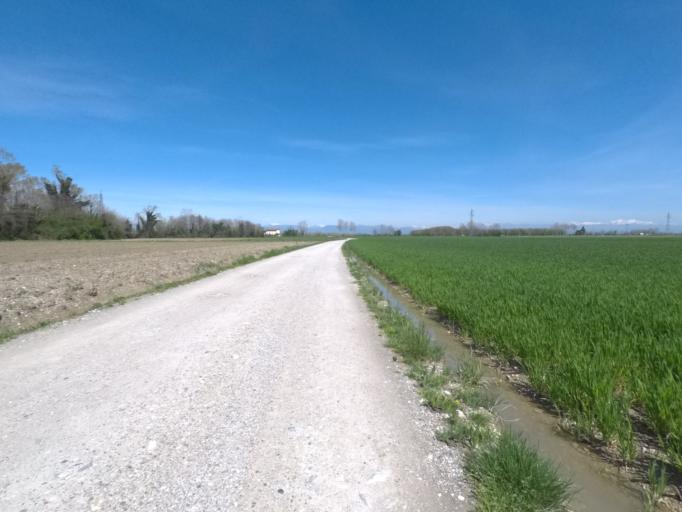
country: IT
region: Friuli Venezia Giulia
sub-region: Provincia di Udine
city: Camino al Tagliamento
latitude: 45.9622
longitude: 12.9165
